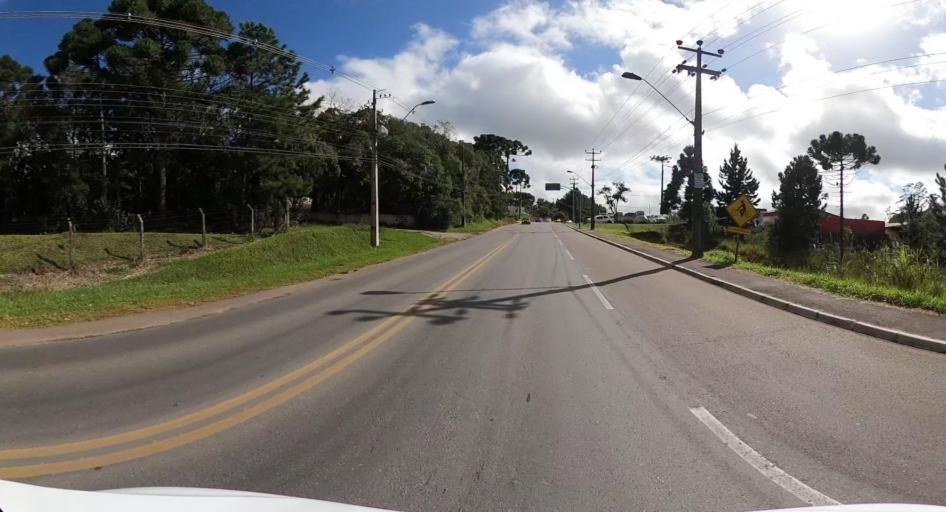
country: BR
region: Parana
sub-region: Quatro Barras
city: Quatro Barras
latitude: -25.3570
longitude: -49.0834
